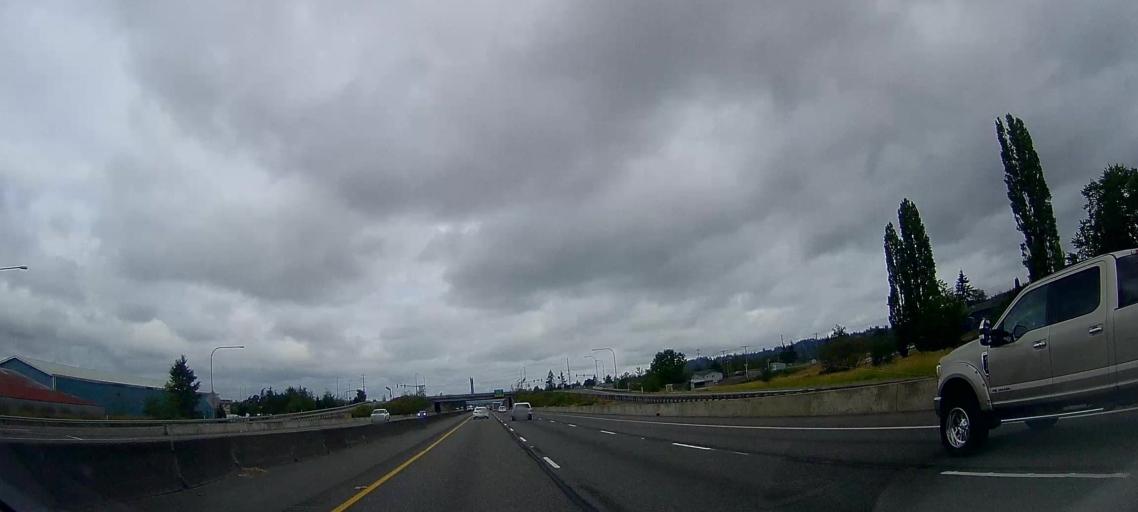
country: US
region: Washington
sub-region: Lewis County
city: Chehalis
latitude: 46.6244
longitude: -122.9305
